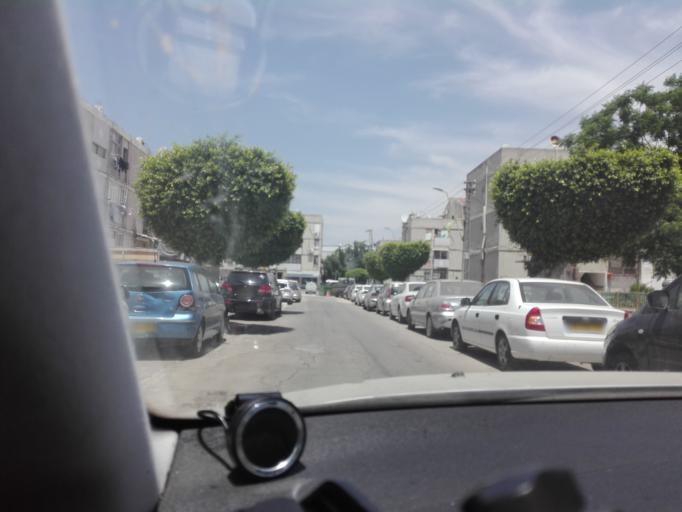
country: IL
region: Central District
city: Bene 'Ayish
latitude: 31.7299
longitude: 34.7509
